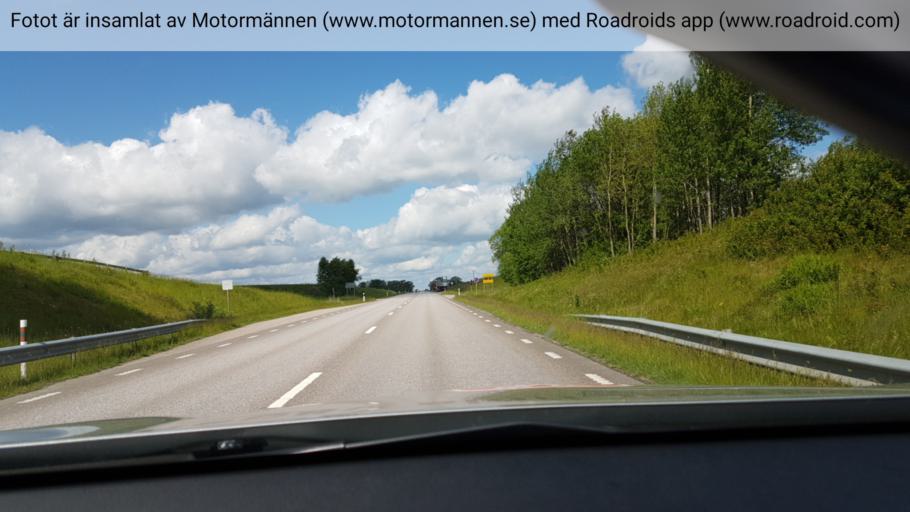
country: SE
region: Vaestra Goetaland
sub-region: Vara Kommun
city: Vara
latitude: 58.2982
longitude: 12.9364
